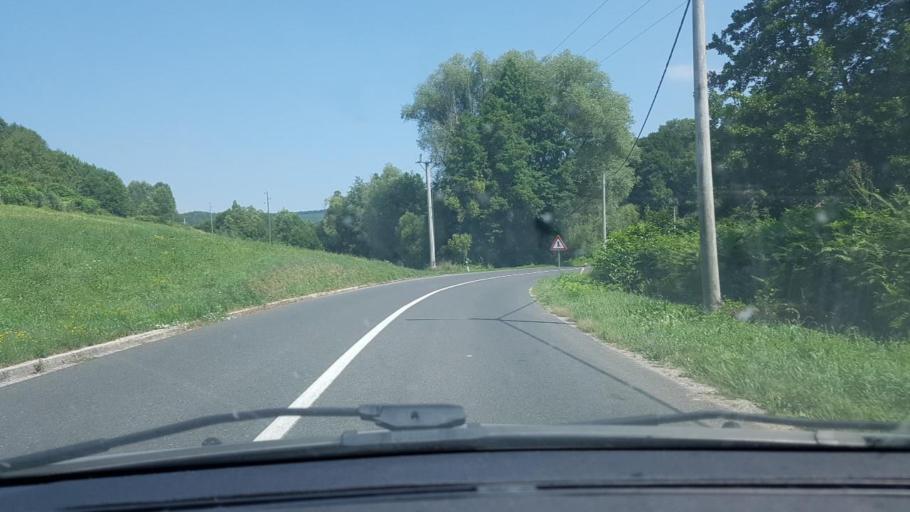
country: BA
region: Federation of Bosnia and Herzegovina
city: Velika Kladusa
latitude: 45.2357
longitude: 15.7354
